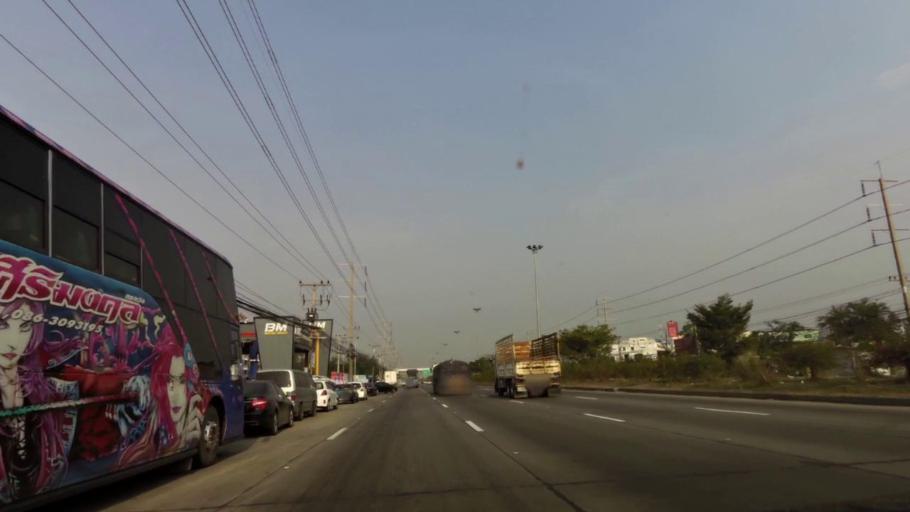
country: TH
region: Phra Nakhon Si Ayutthaya
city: Phra Nakhon Si Ayutthaya
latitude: 14.3279
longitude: 100.6254
